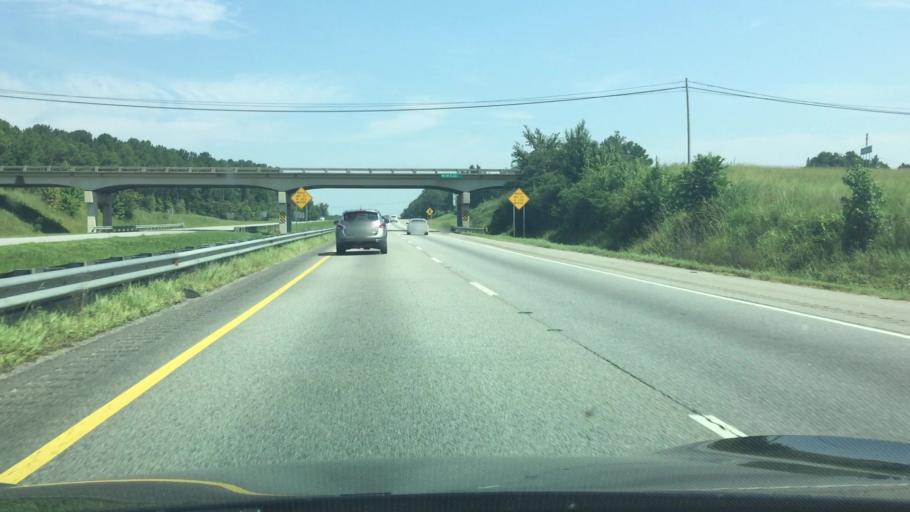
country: US
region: Alabama
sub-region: Shelby County
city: Calera
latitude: 33.1024
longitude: -86.7389
